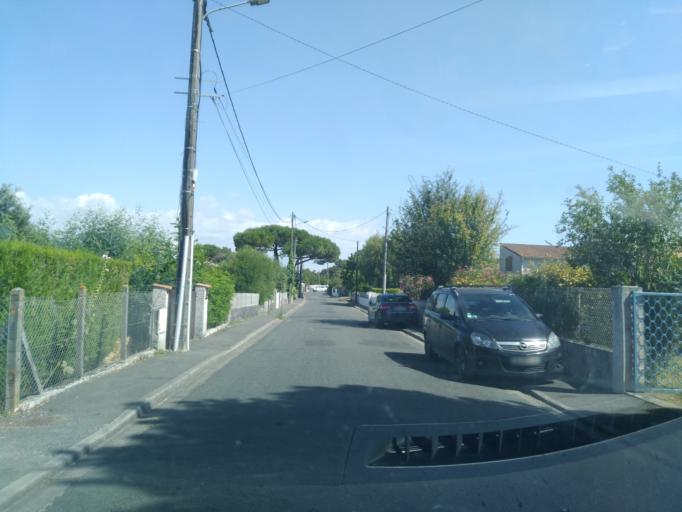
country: FR
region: Poitou-Charentes
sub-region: Departement de la Charente-Maritime
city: Saint-Palais-sur-Mer
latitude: 45.6461
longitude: -1.0824
